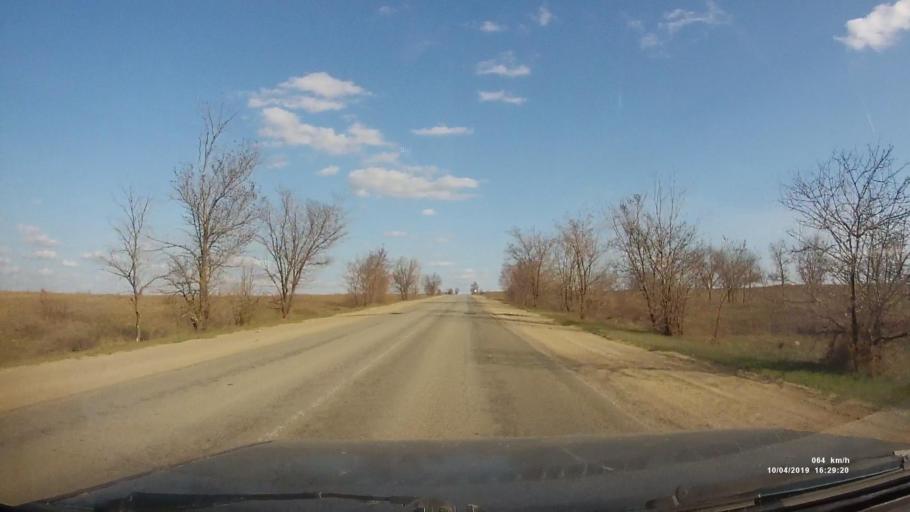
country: RU
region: Rostov
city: Staraya Stanitsa
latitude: 48.2690
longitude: 40.3540
